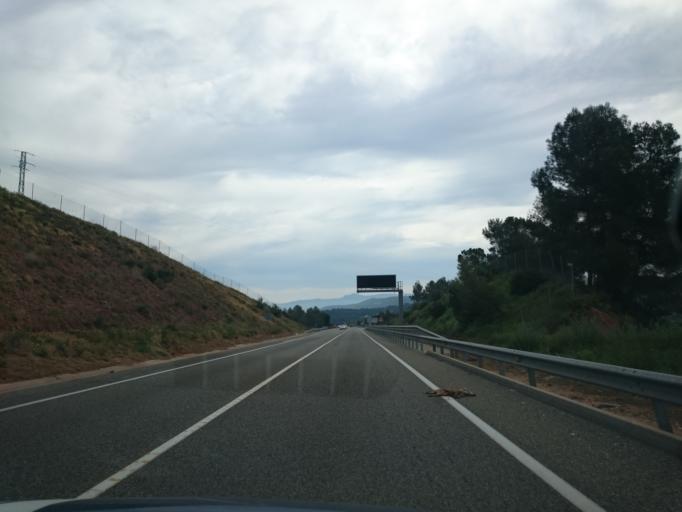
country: ES
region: Catalonia
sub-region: Provincia de Barcelona
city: Sant Salvador de Guardiola
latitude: 41.6896
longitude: 1.7671
